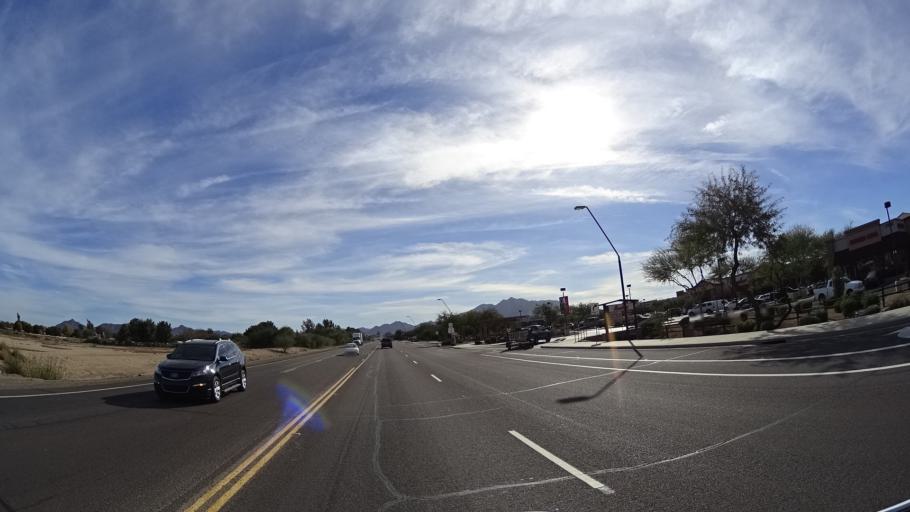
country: US
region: Arizona
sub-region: Maricopa County
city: Queen Creek
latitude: 33.2340
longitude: -111.6859
